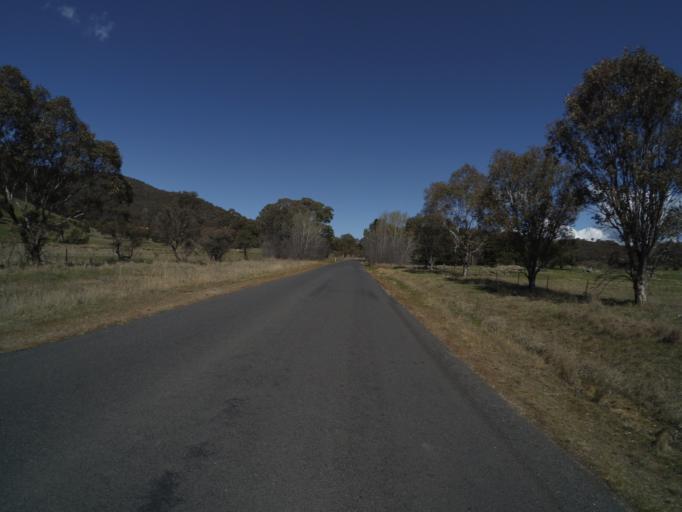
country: AU
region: Australian Capital Territory
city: Macquarie
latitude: -35.1648
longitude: 148.8863
